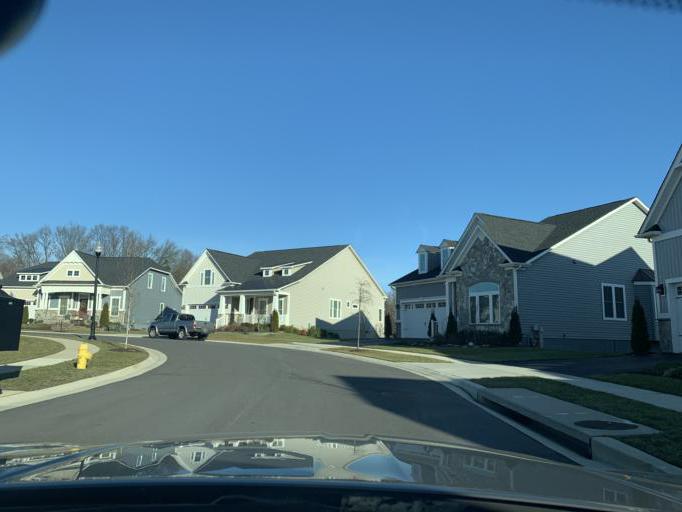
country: US
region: Maryland
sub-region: Anne Arundel County
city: Crofton
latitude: 39.0243
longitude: -76.7217
